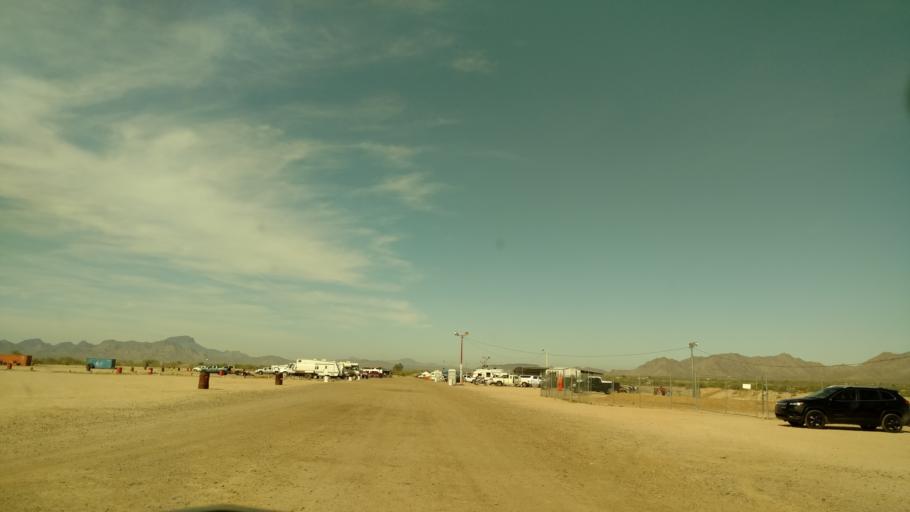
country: US
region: Arizona
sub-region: Maricopa County
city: Buckeye
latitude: 33.2153
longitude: -112.6600
